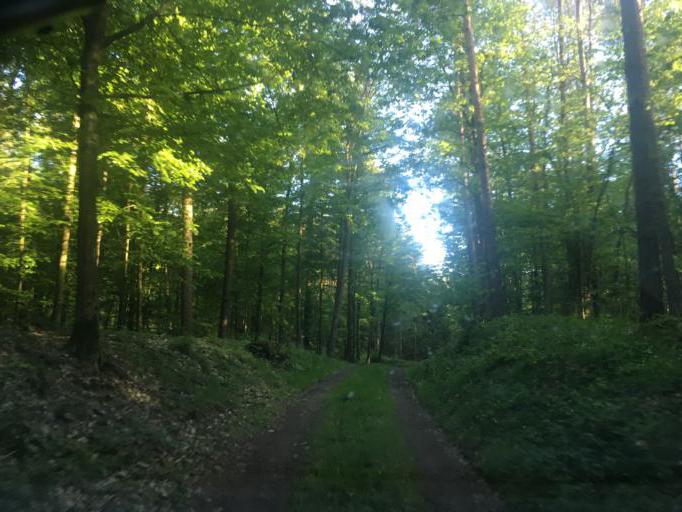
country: PL
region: Kujawsko-Pomorskie
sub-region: Powiat brodnicki
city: Gorzno
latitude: 53.2109
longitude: 19.7211
